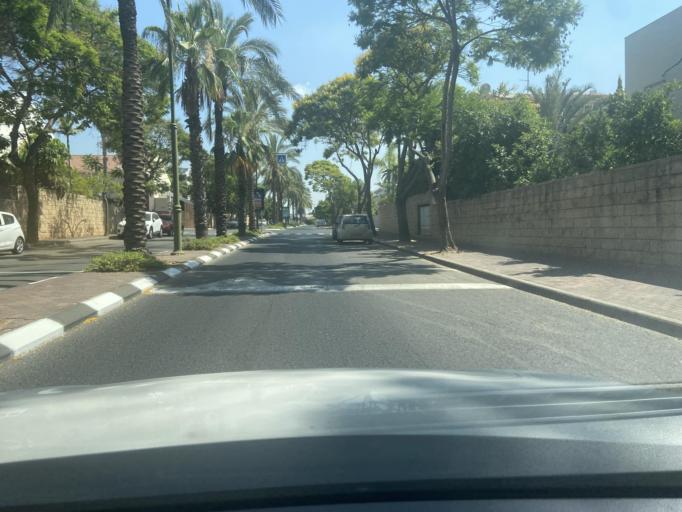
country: IL
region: Central District
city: Yehud
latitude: 32.0361
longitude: 34.8819
